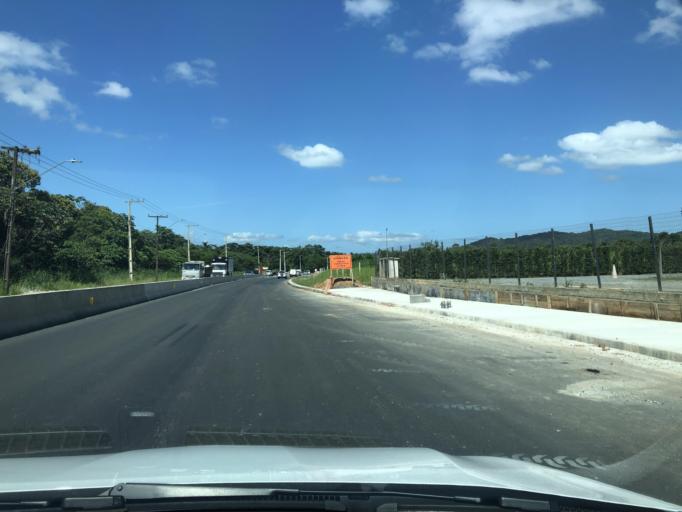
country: BR
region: Santa Catarina
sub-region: Joinville
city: Joinville
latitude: -26.2513
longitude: -48.8663
